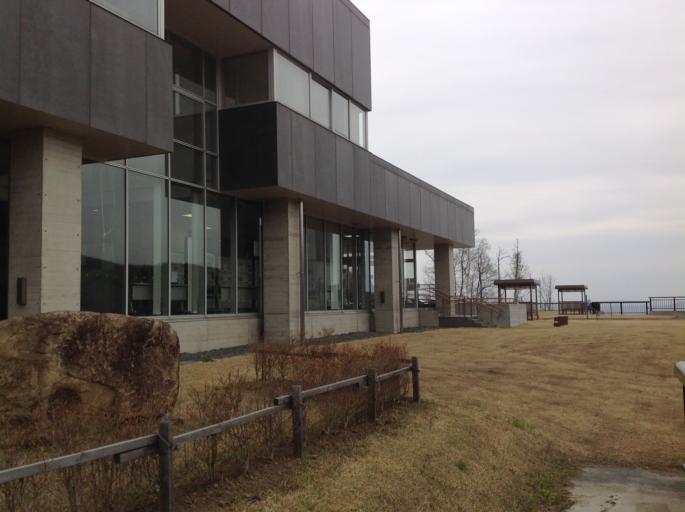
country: JP
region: Iwate
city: Mizusawa
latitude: 39.1250
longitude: 140.9197
